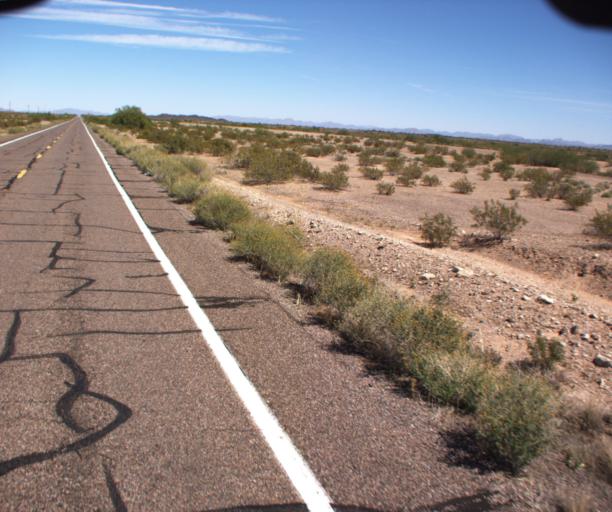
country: US
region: Arizona
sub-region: Maricopa County
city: Gila Bend
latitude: 32.7754
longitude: -112.8133
